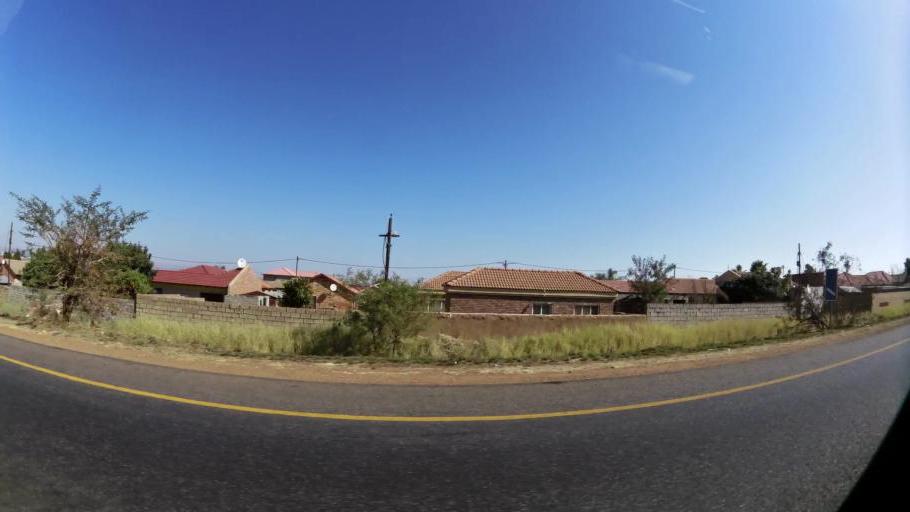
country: ZA
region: Gauteng
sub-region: City of Tshwane Metropolitan Municipality
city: Mabopane
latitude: -25.5853
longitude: 28.1107
